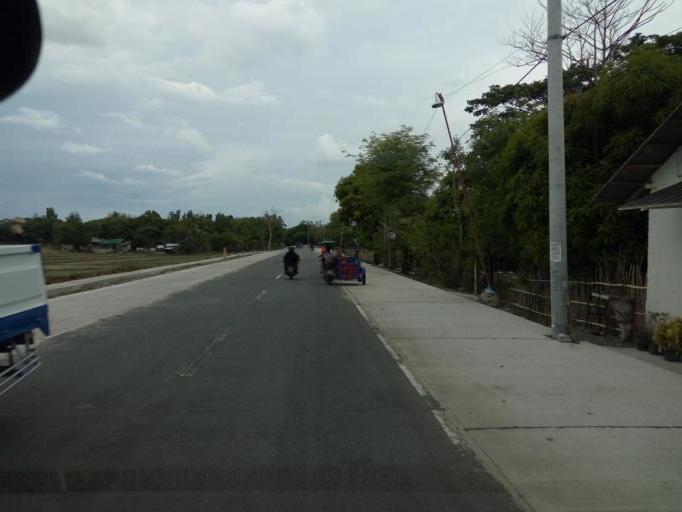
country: PH
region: Central Luzon
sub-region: Province of Nueva Ecija
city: Parista
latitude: 15.8444
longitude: 120.9347
